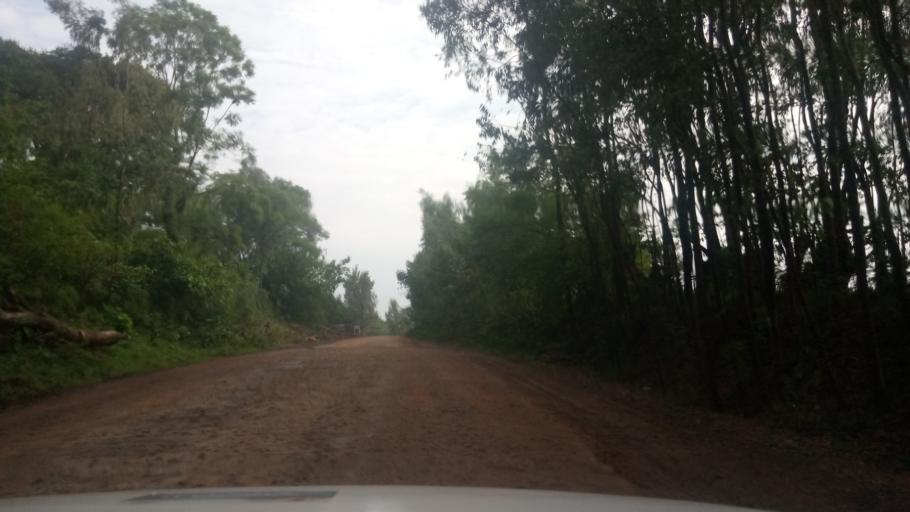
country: ET
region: Oromiya
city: Agaro
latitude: 7.8461
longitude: 36.6575
